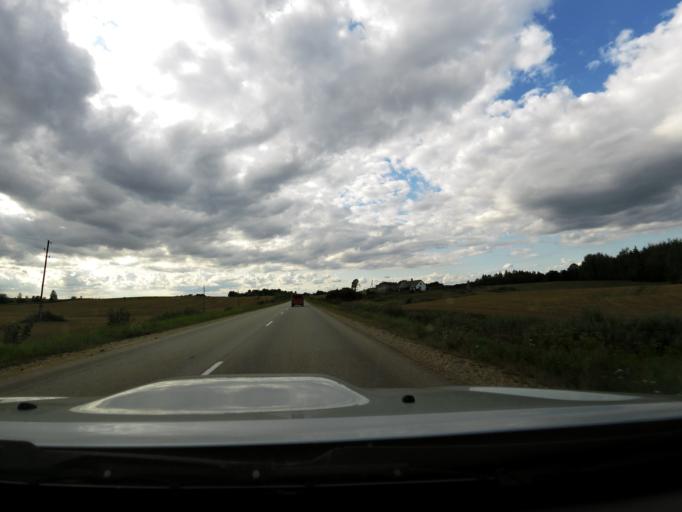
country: LV
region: Ilukste
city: Ilukste
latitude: 55.9728
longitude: 26.0242
